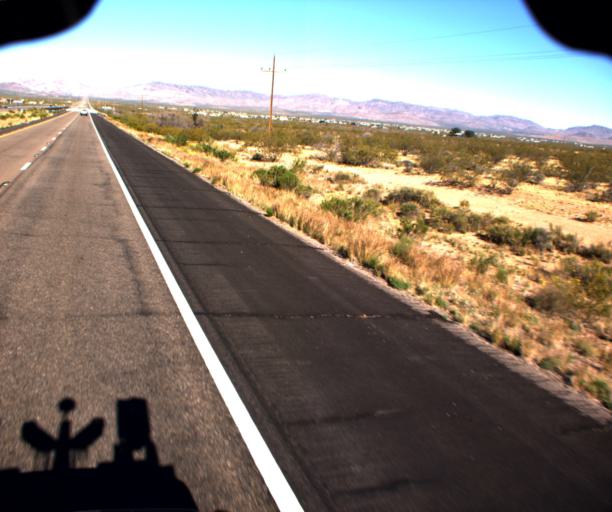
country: US
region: Arizona
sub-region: Mohave County
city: Golden Valley
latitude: 35.2251
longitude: -114.2762
